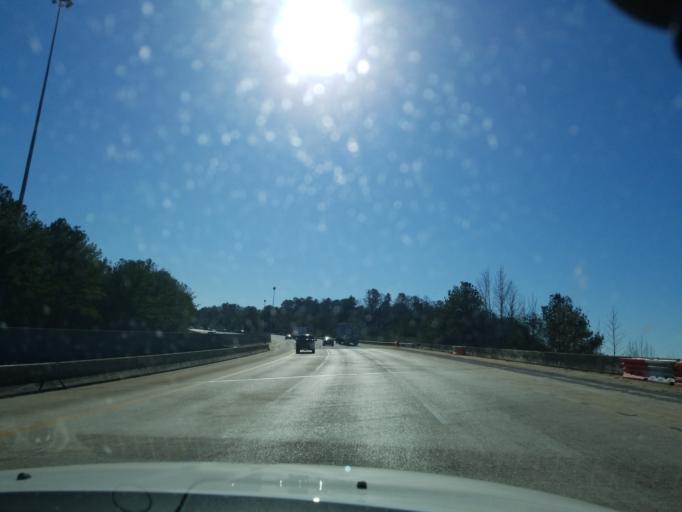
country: US
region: Alabama
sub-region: Jefferson County
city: Cahaba Heights
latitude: 33.4853
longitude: -86.7099
